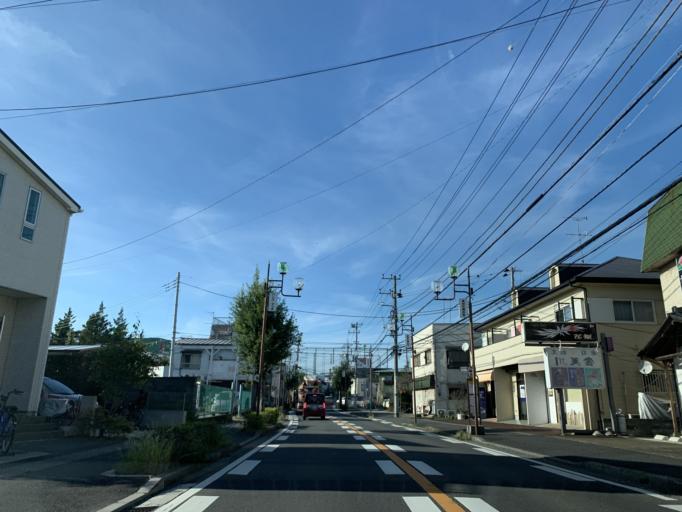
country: JP
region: Chiba
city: Nagareyama
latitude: 35.8855
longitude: 139.9211
